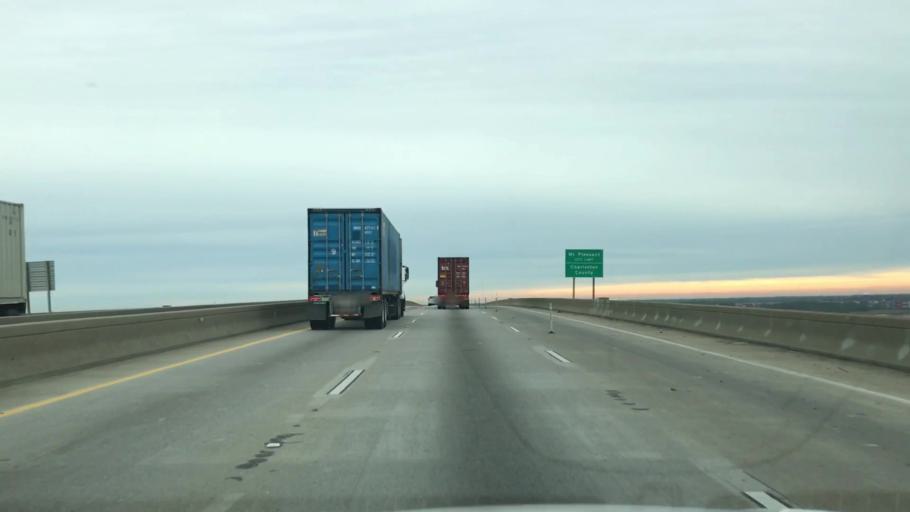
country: US
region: South Carolina
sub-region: Charleston County
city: Mount Pleasant
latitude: 32.8599
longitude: -79.8964
